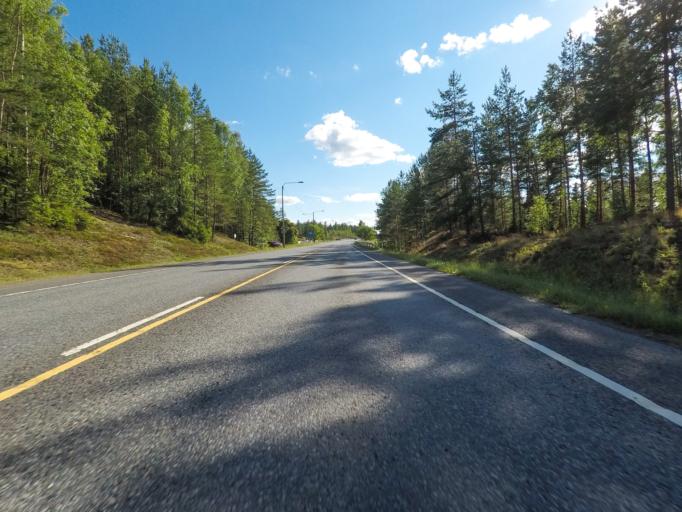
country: FI
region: Uusimaa
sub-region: Helsinki
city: Vihti
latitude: 60.3268
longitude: 24.2772
